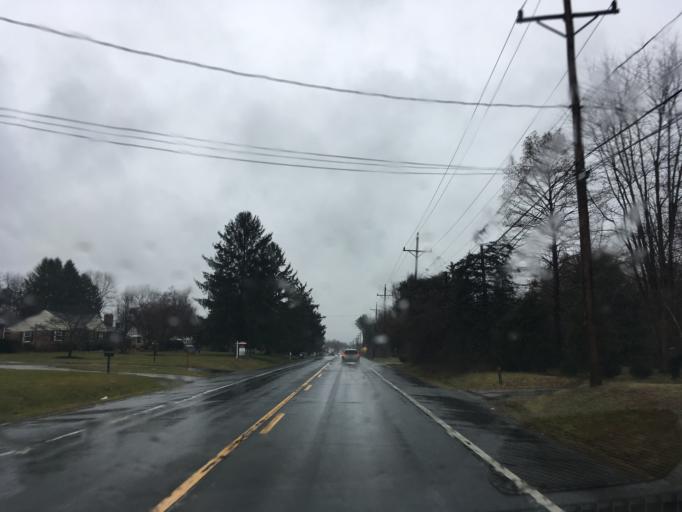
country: US
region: Delaware
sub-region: New Castle County
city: Bellefonte
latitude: 39.7955
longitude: -75.5054
